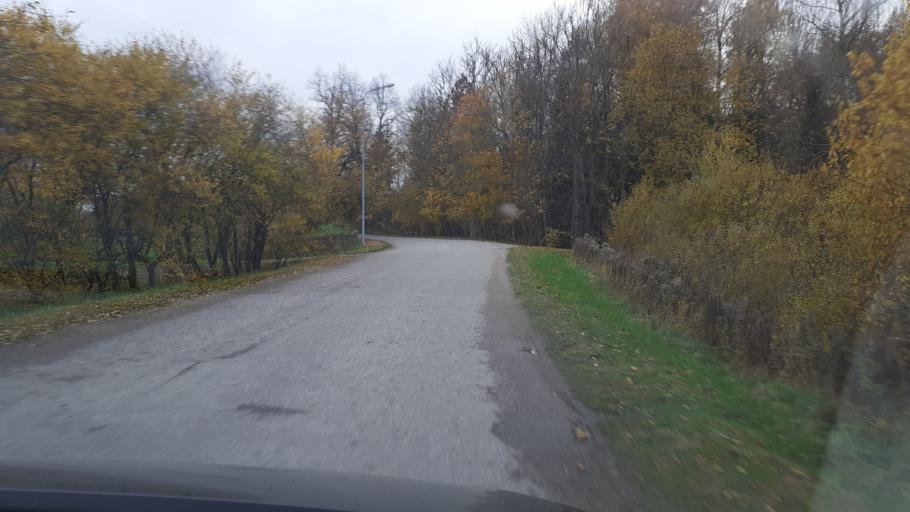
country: LV
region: Kuldigas Rajons
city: Kuldiga
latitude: 56.9826
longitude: 22.0199
